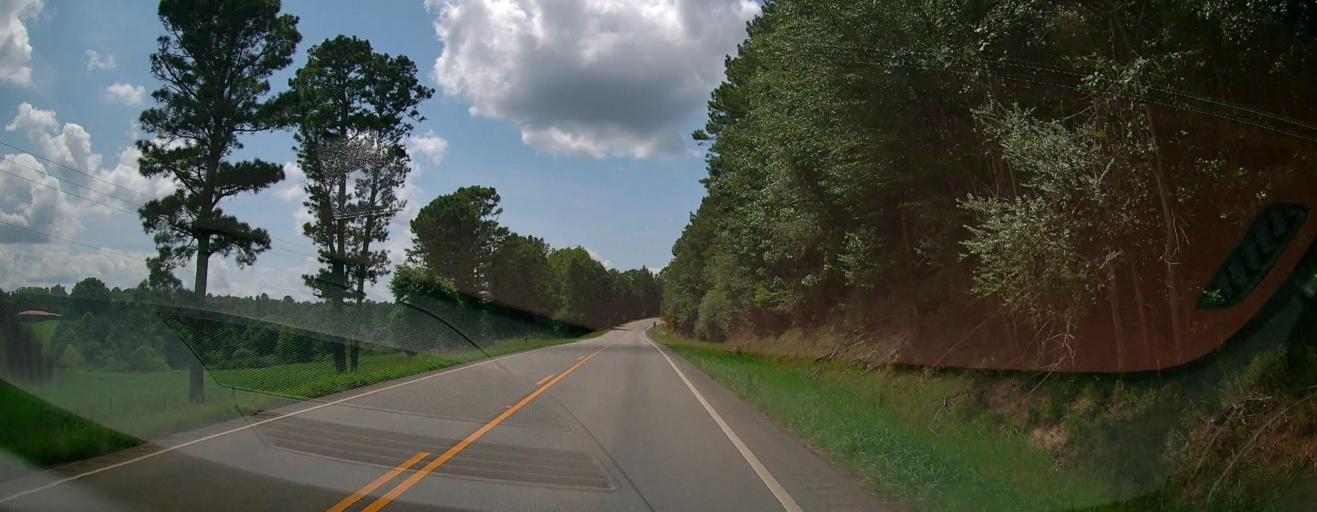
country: US
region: Alabama
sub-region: Cleburne County
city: Heflin
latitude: 33.5825
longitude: -85.4714
